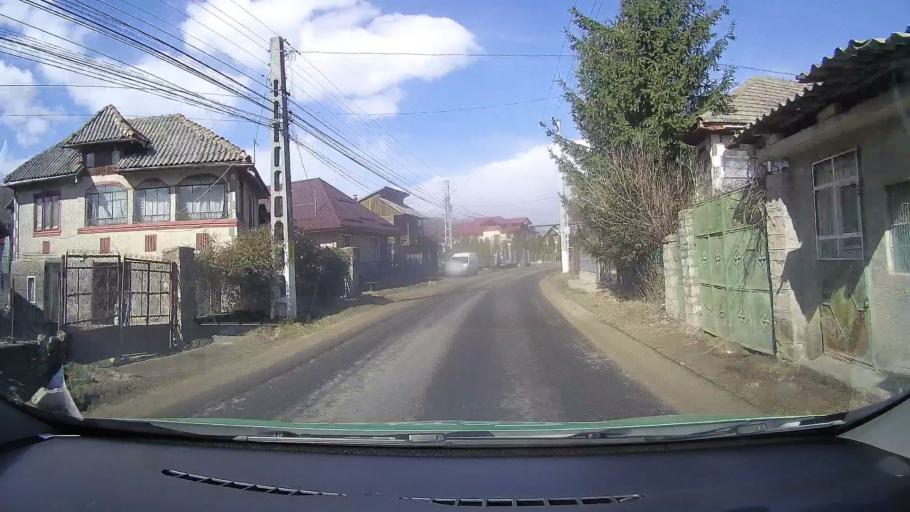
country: RO
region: Dambovita
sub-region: Comuna Runcu
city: Runcu
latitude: 45.1717
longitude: 25.3930
